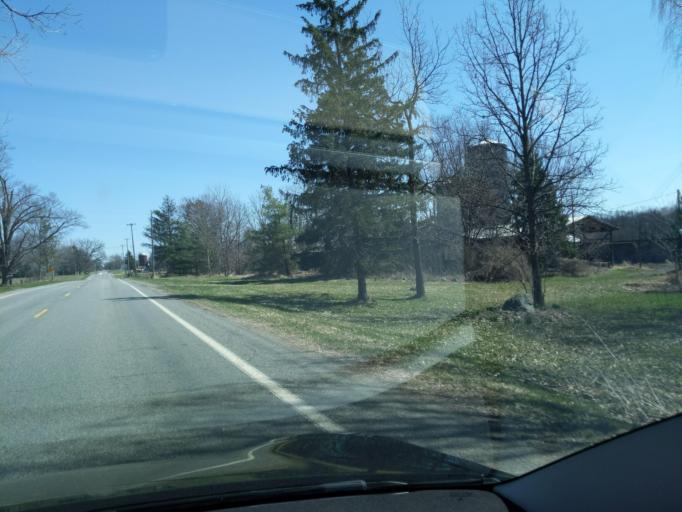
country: US
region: Michigan
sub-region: Ingham County
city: Holt
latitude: 42.5821
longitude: -84.5575
